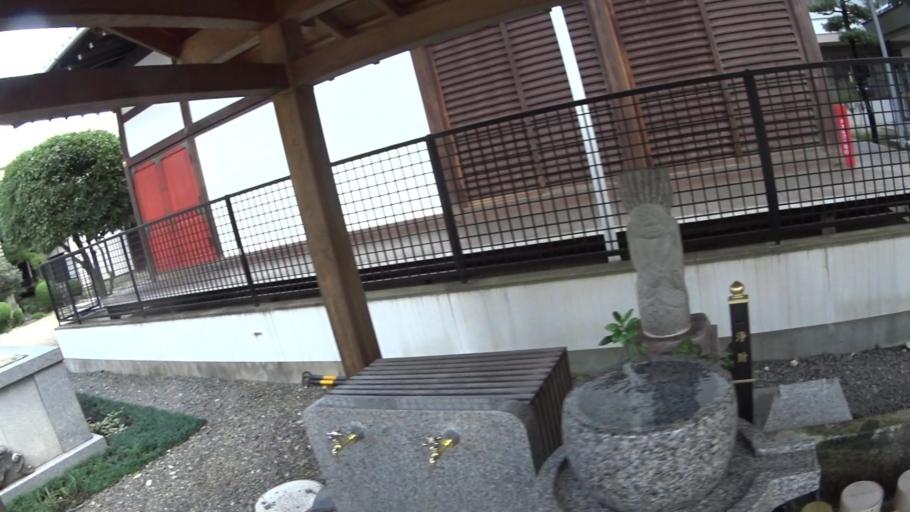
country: JP
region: Kyoto
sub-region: Kyoto-shi
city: Kamigyo-ku
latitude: 35.0253
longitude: 135.7680
